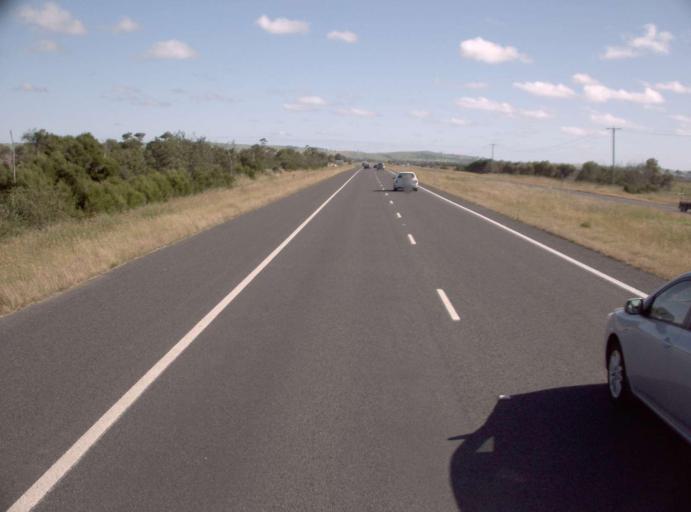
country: AU
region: Victoria
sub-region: Bass Coast
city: North Wonthaggi
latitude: -38.4466
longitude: 145.4826
